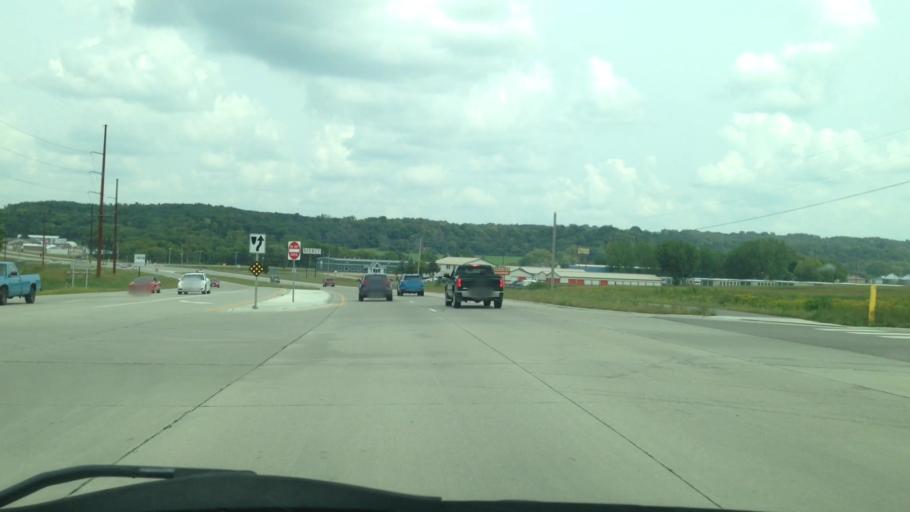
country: US
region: Minnesota
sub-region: Olmsted County
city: Rochester
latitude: 44.0673
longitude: -92.4494
